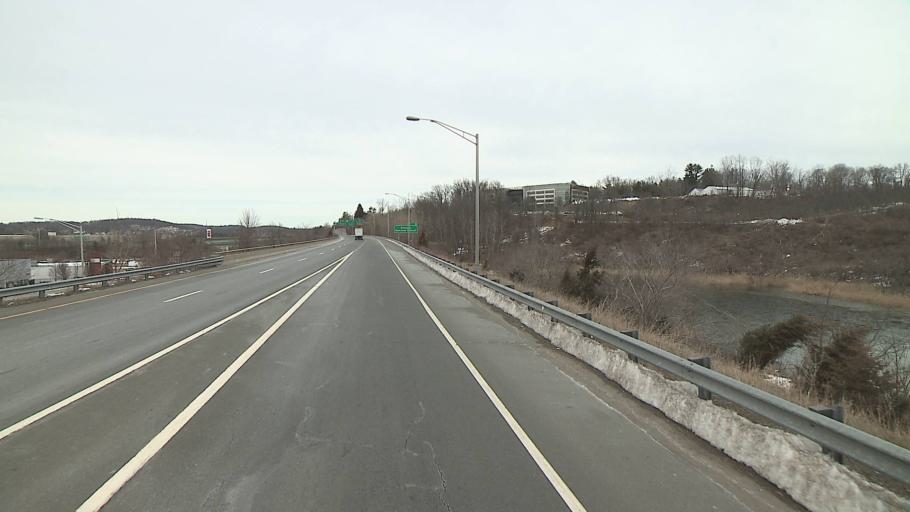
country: US
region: Connecticut
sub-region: Fairfield County
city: Danbury
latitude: 41.3739
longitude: -73.4731
